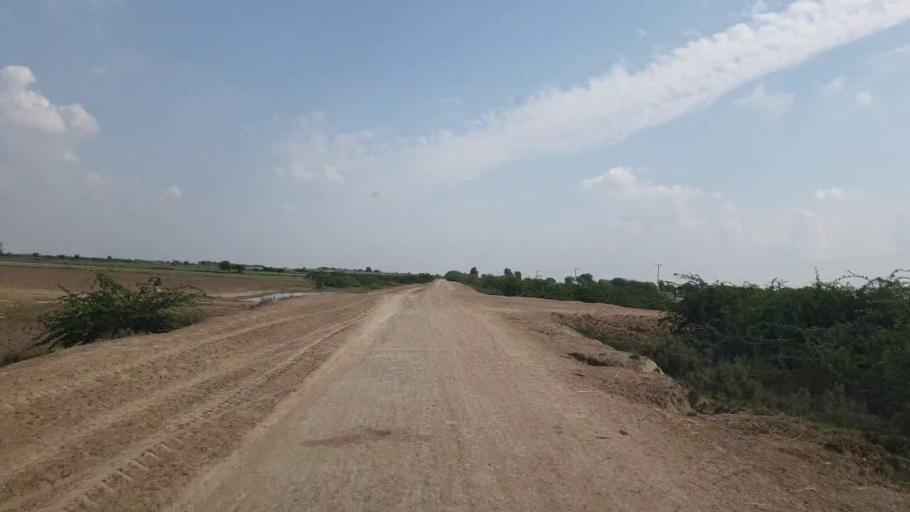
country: PK
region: Sindh
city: Badin
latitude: 24.4774
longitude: 68.6274
